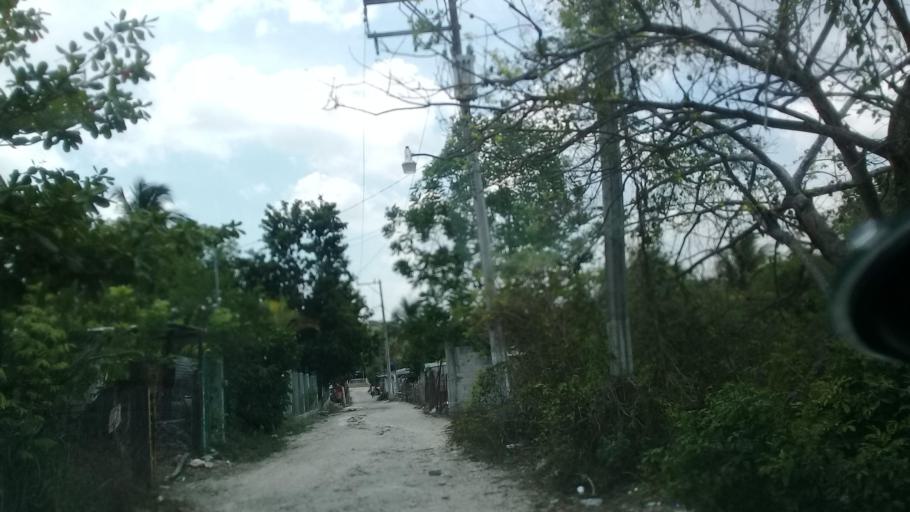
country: MX
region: Veracruz
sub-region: Emiliano Zapata
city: Plan del Rio
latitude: 19.4046
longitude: -96.6539
